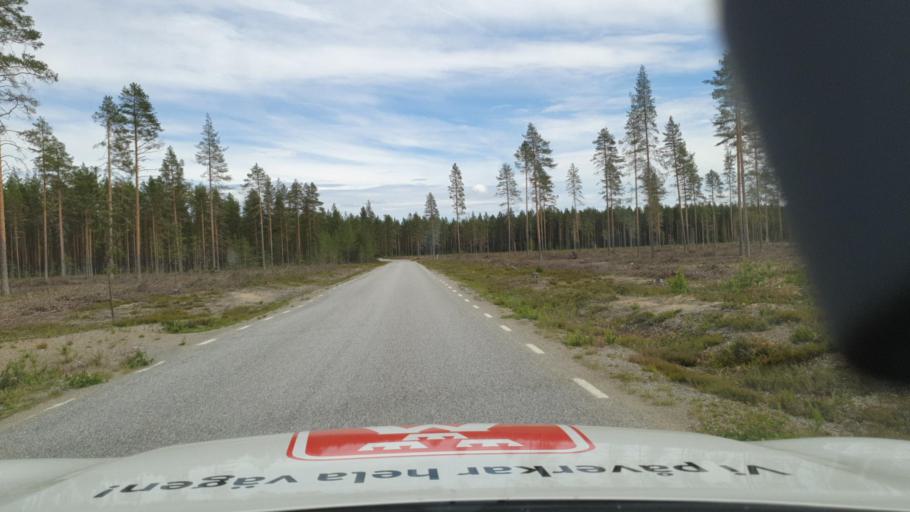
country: SE
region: Vaesterbotten
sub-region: Skelleftea Kommun
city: Burtraesk
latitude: 64.5021
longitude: 20.8374
